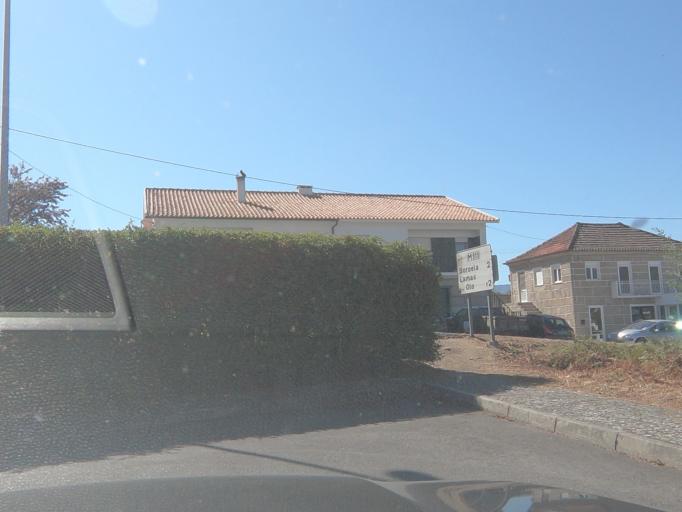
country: PT
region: Vila Real
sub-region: Vila Real
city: Vila Real
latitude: 41.3156
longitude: -7.7354
